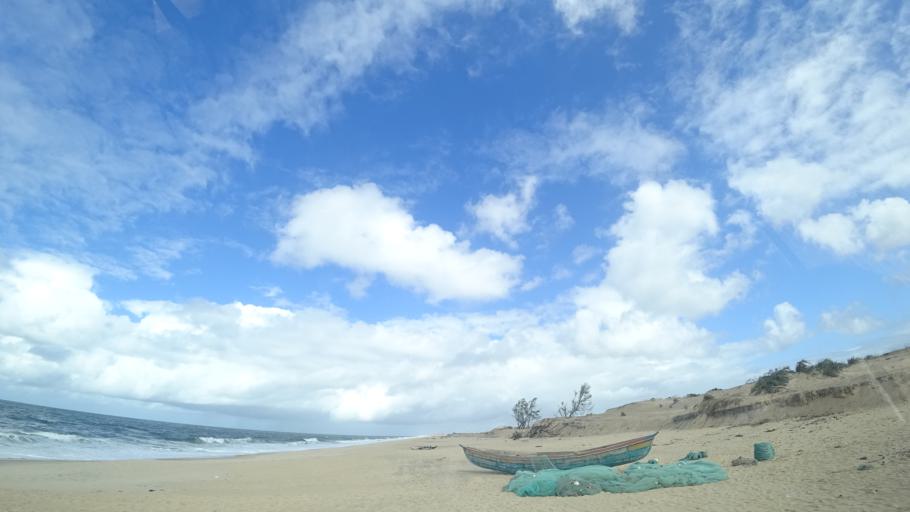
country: MZ
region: Sofala
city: Beira
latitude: -19.6473
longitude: 35.1828
